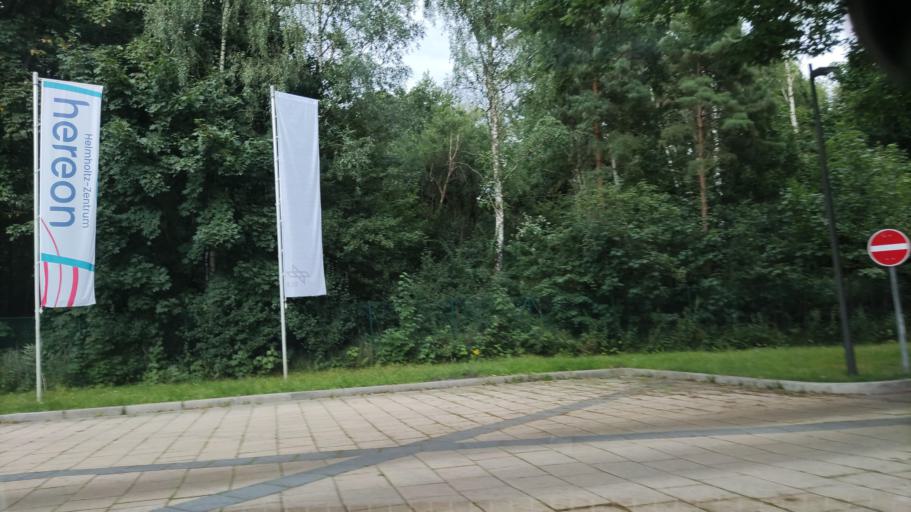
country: DE
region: Lower Saxony
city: Tespe
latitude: 53.4107
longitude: 10.4227
